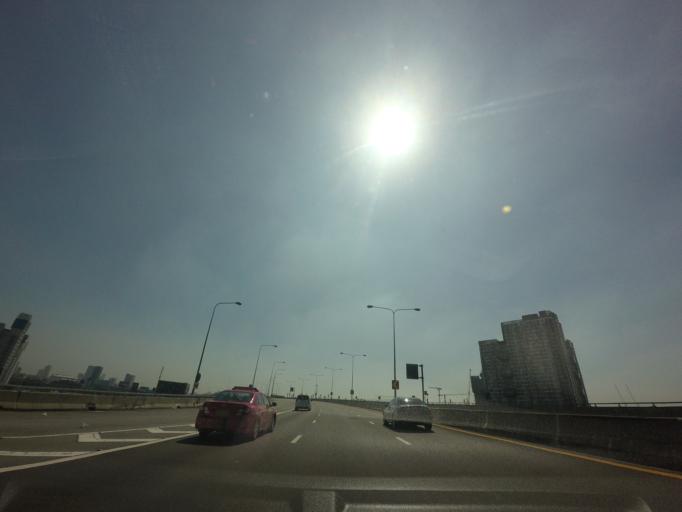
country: TH
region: Bangkok
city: Phra Khanong
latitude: 13.6748
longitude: 100.6050
